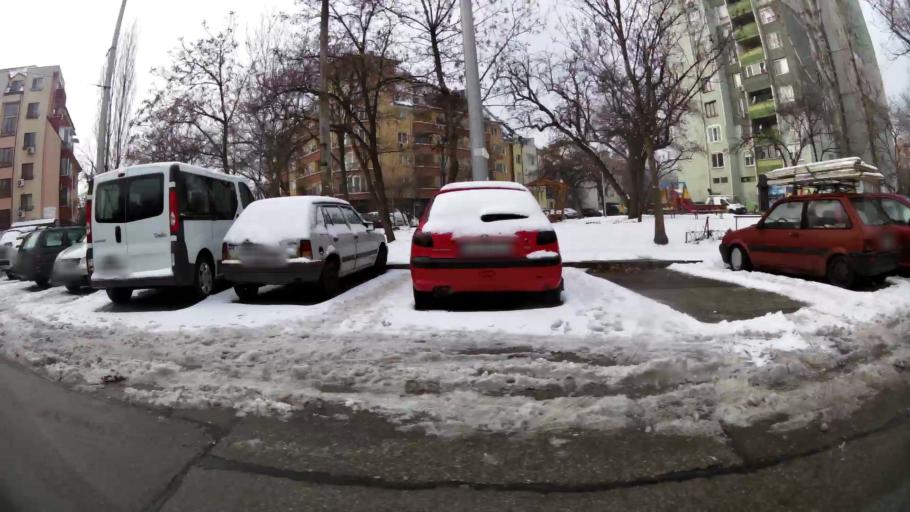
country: BG
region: Sofia-Capital
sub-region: Stolichna Obshtina
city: Sofia
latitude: 42.7088
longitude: 23.3111
